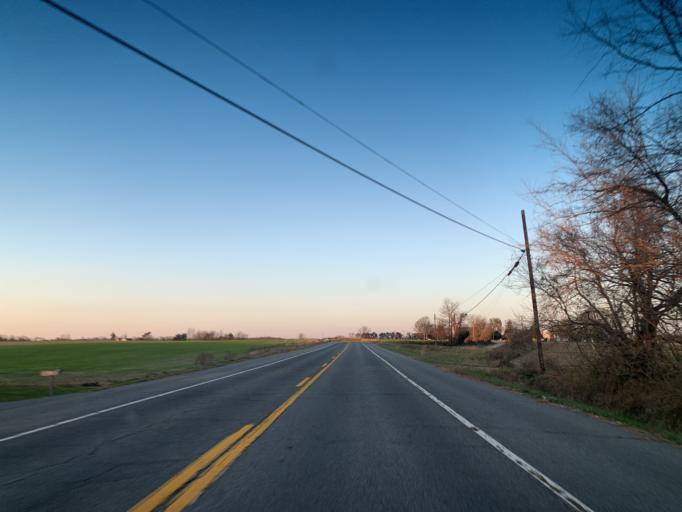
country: US
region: Maryland
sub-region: Cecil County
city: Charlestown
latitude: 39.4212
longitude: -75.9182
